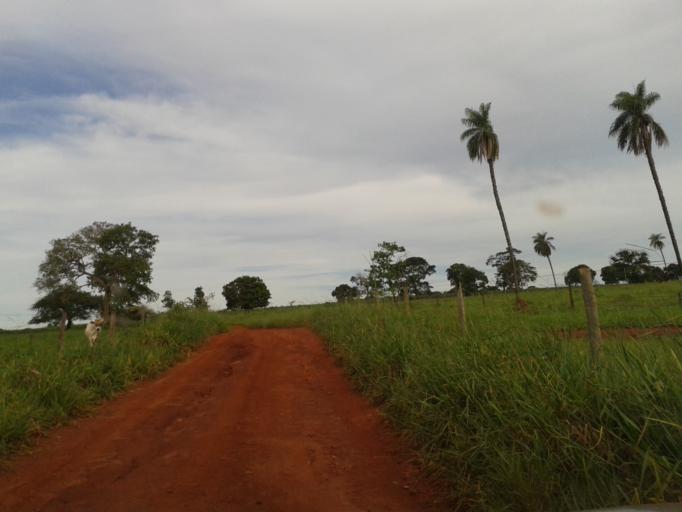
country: BR
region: Minas Gerais
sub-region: Capinopolis
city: Capinopolis
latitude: -18.7946
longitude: -49.8311
